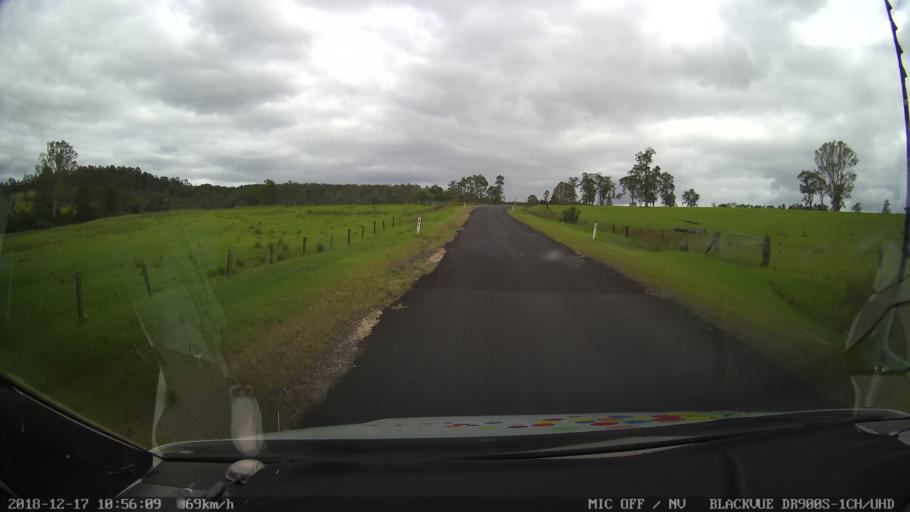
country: AU
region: New South Wales
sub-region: Richmond Valley
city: Casino
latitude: -28.8238
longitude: 152.5854
